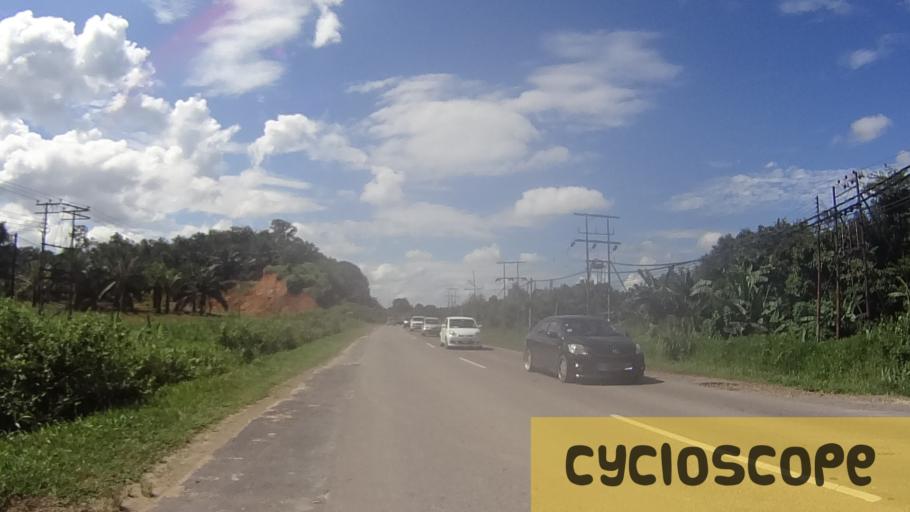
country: MY
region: Sabah
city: Beaufort
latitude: 5.3217
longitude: 115.7131
